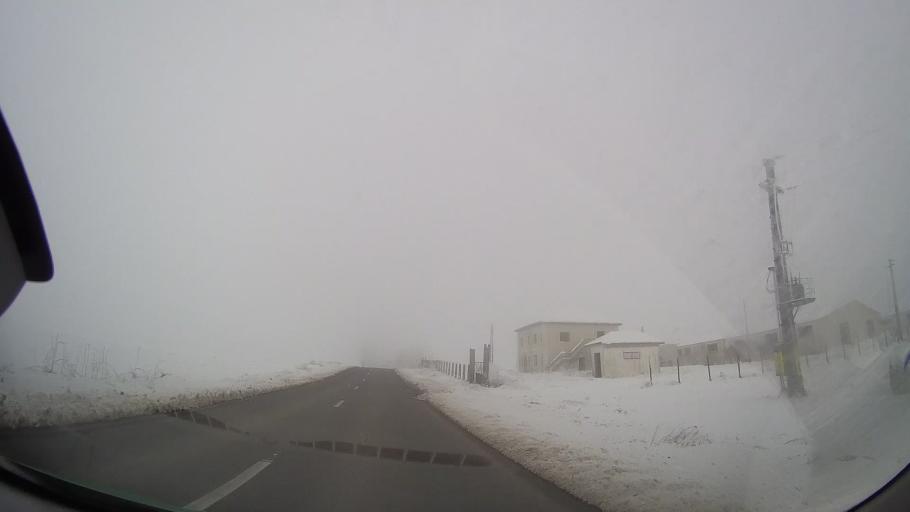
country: RO
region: Iasi
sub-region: Comuna Mogosesti-Siret
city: Mogosesti-Siret
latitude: 47.1461
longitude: 26.7786
